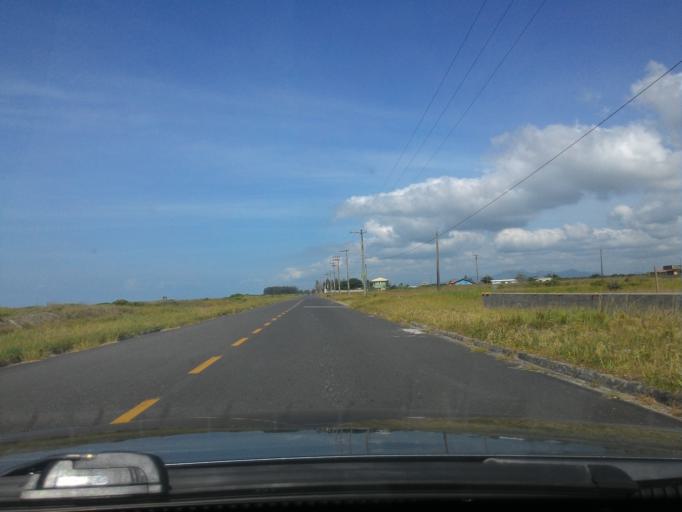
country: BR
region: Sao Paulo
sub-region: Iguape
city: Iguape
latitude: -24.7760
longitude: -47.5941
